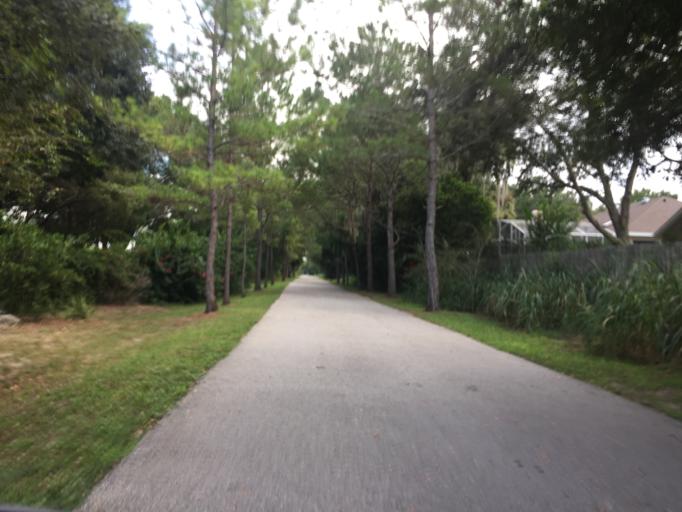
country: US
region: Florida
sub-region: Seminole County
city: Oviedo
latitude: 28.6789
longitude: -81.2198
